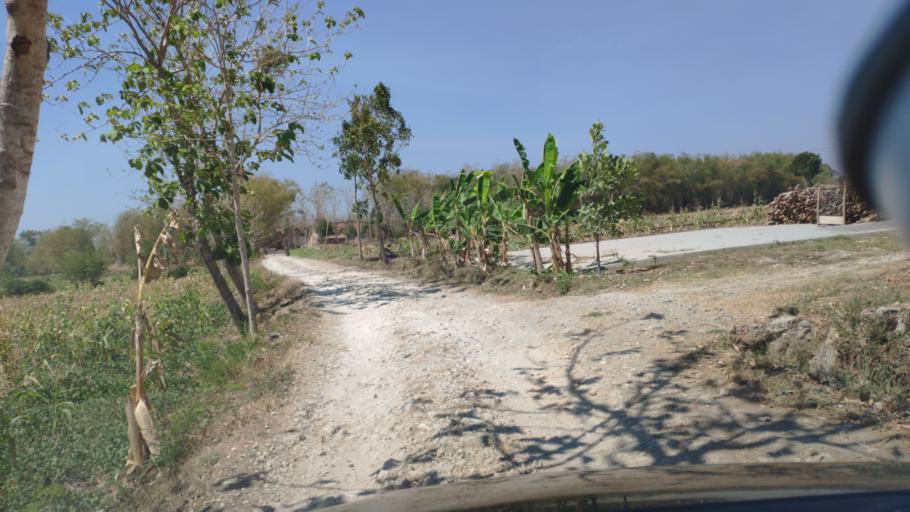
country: ID
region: Central Java
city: Mojo Wetan
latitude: -7.0352
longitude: 111.3601
